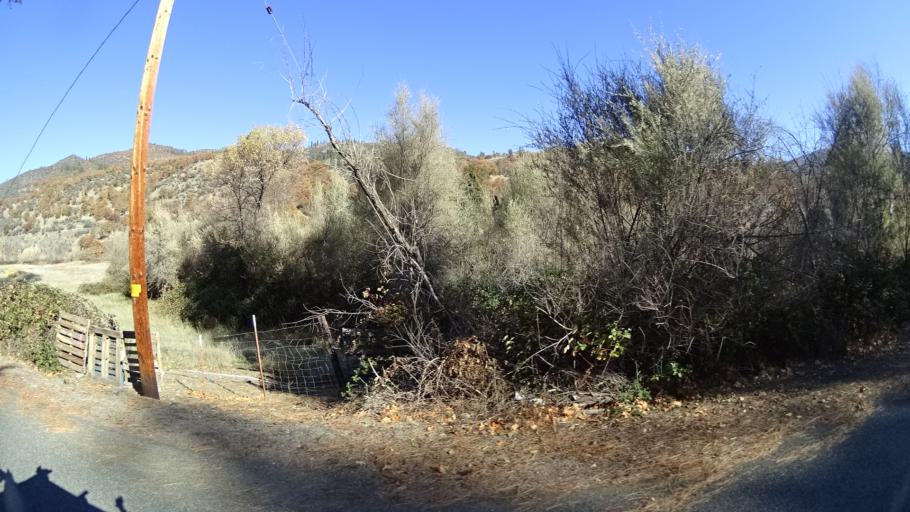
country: US
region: California
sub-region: Siskiyou County
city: Yreka
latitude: 41.8337
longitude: -122.8536
